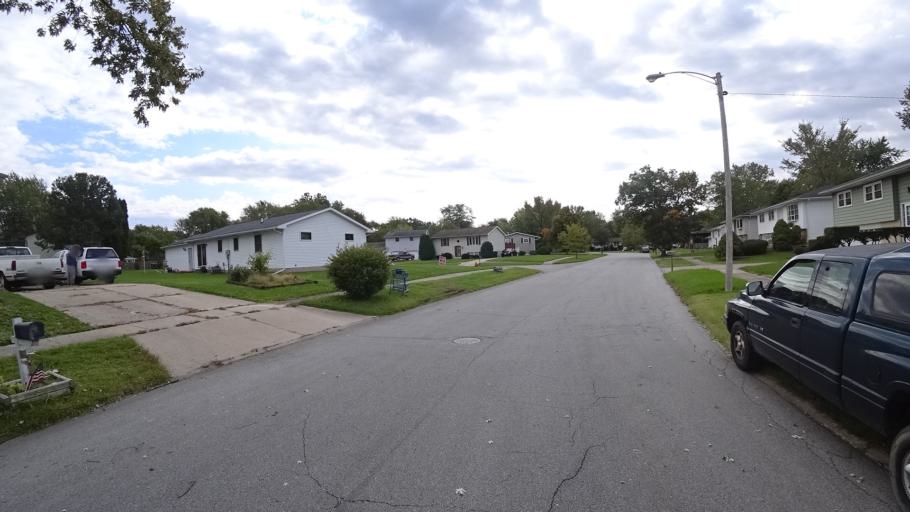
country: US
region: Indiana
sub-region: LaPorte County
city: Michigan City
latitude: 41.6731
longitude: -86.9015
